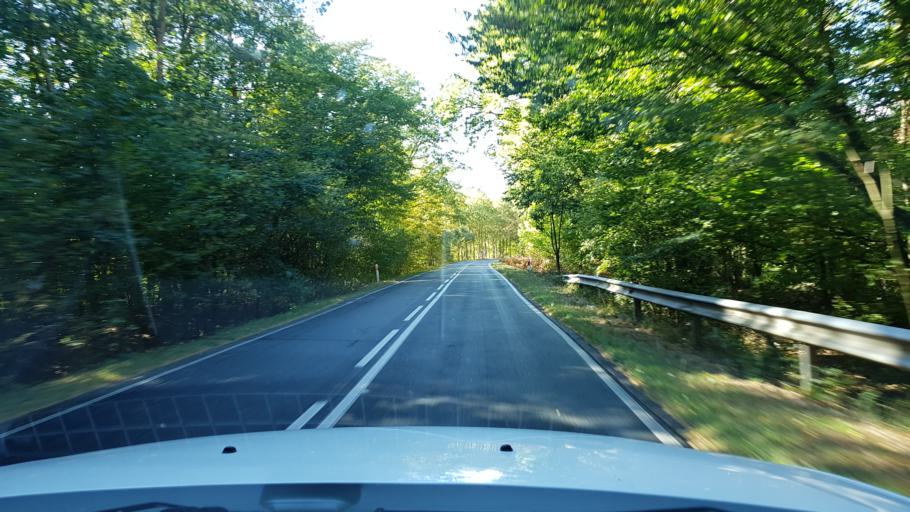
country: PL
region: West Pomeranian Voivodeship
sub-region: Powiat gryfinski
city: Gryfino
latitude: 53.2002
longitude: 14.5101
